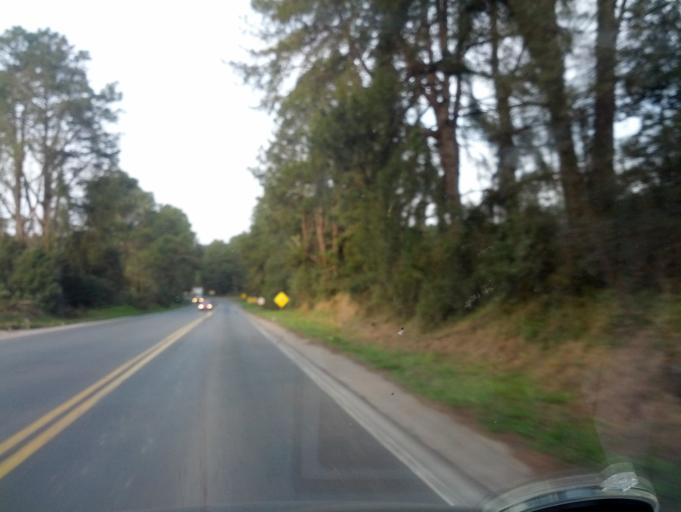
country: BR
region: Santa Catarina
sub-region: Otacilio Costa
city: Otacilio Costa
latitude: -27.3039
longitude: -50.0905
